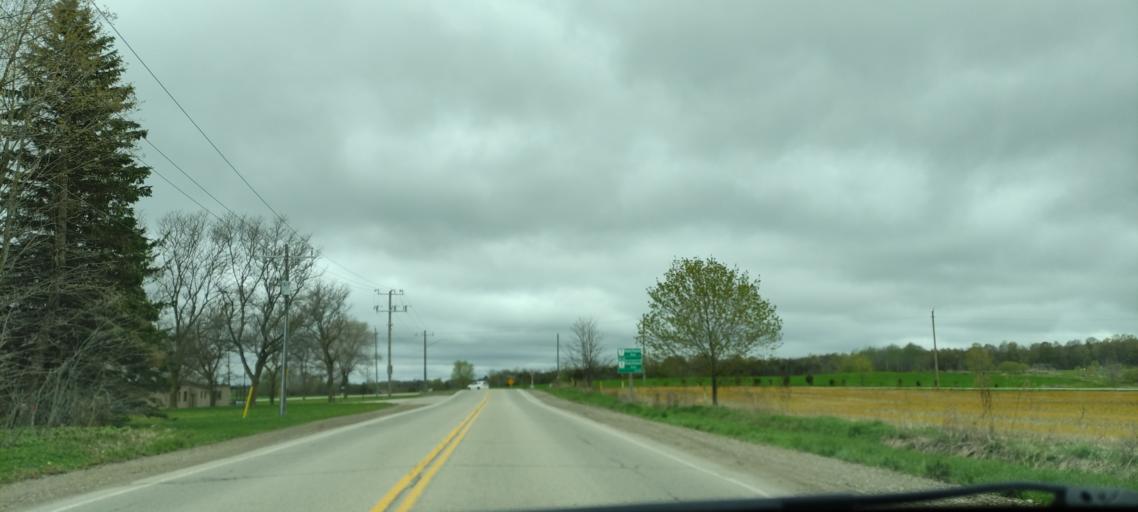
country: CA
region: Ontario
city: Stratford
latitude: 43.4787
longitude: -80.7778
